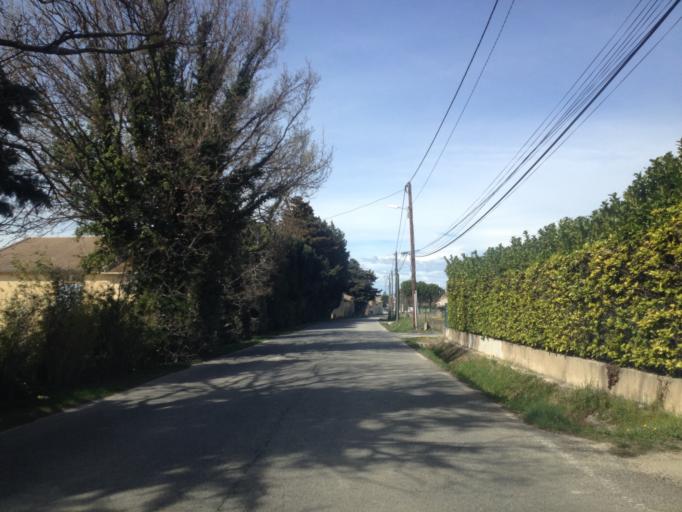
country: FR
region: Provence-Alpes-Cote d'Azur
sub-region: Departement du Vaucluse
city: Camaret-sur-Aigues
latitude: 44.1630
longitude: 4.8830
